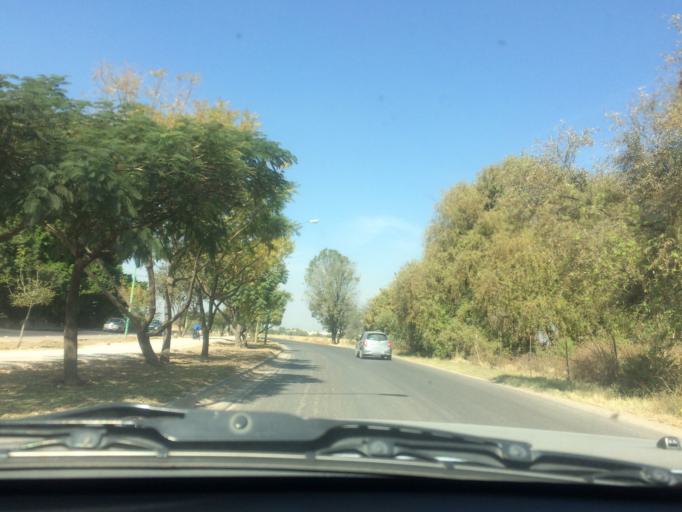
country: MX
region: Guanajuato
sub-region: Leon
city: Fraccionamiento Paraiso Real
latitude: 21.1193
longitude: -101.6114
